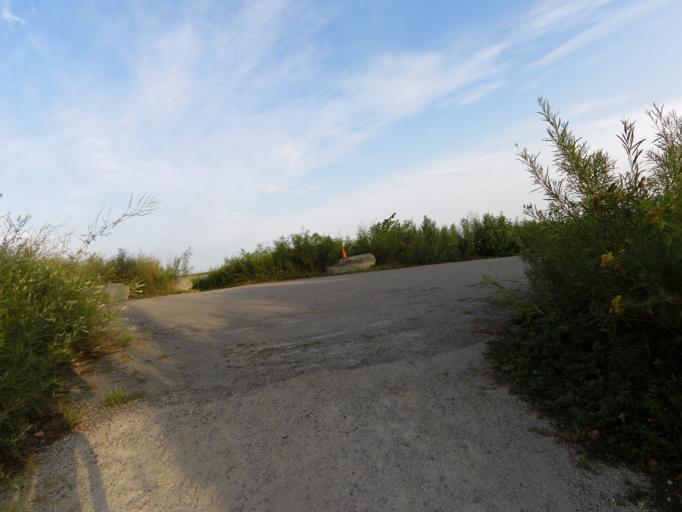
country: CA
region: Ontario
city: Toronto
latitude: 43.6259
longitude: -79.3323
